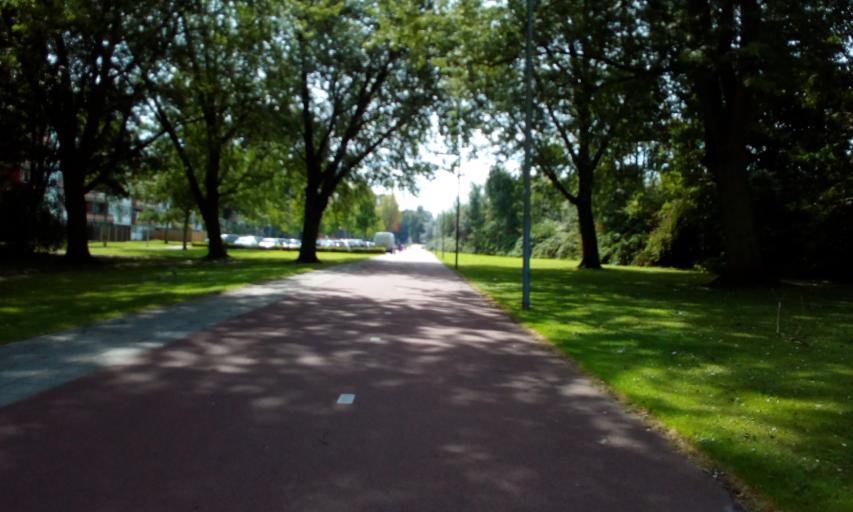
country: NL
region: South Holland
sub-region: Gemeente Rotterdam
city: Rotterdam
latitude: 51.9506
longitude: 4.4638
